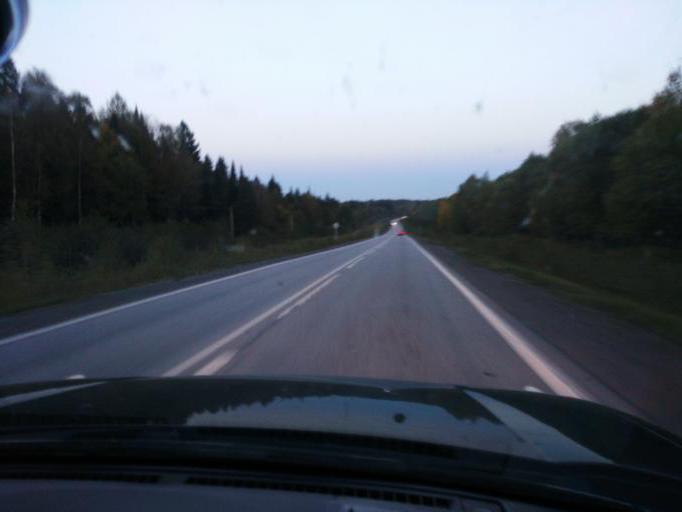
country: RU
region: Perm
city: Verkhnechusovskiye Gorodki
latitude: 58.2592
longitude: 56.9865
